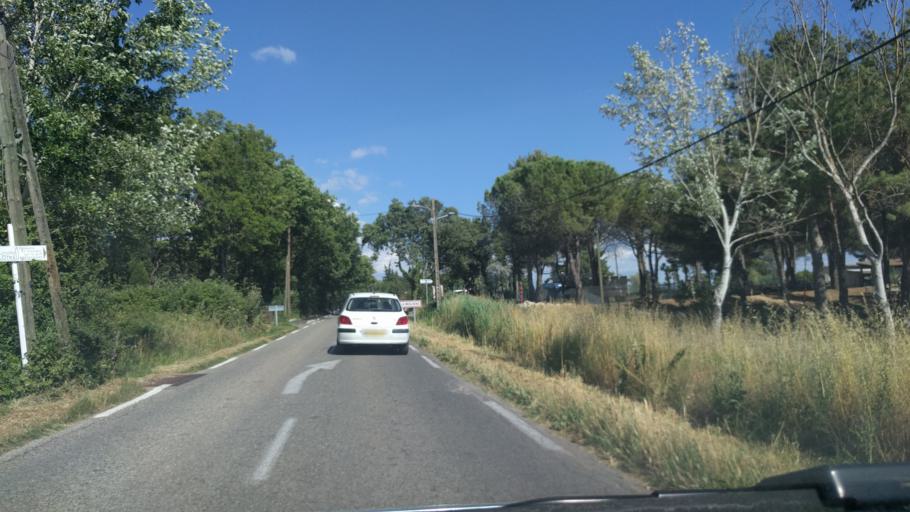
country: FR
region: Provence-Alpes-Cote d'Azur
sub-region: Departement des Bouches-du-Rhone
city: Eguilles
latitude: 43.5251
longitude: 5.3884
